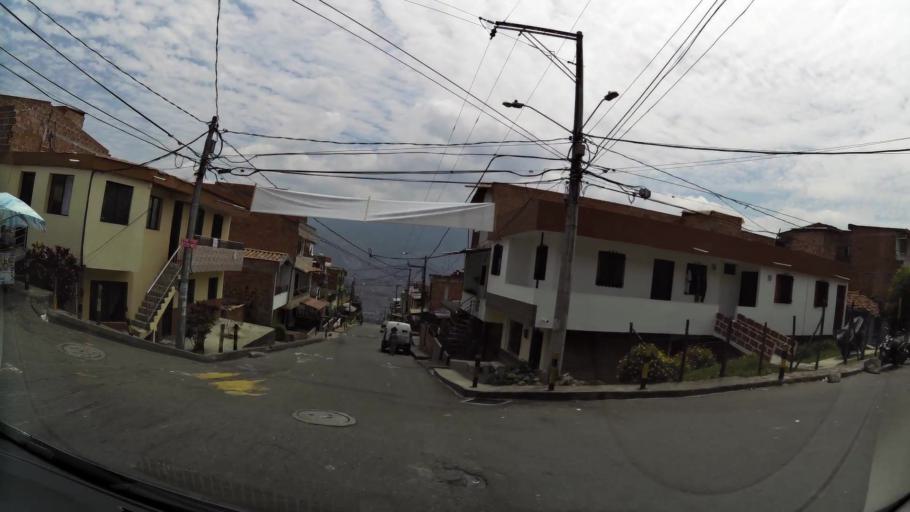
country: CO
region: Antioquia
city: Bello
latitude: 6.3128
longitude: -75.5808
